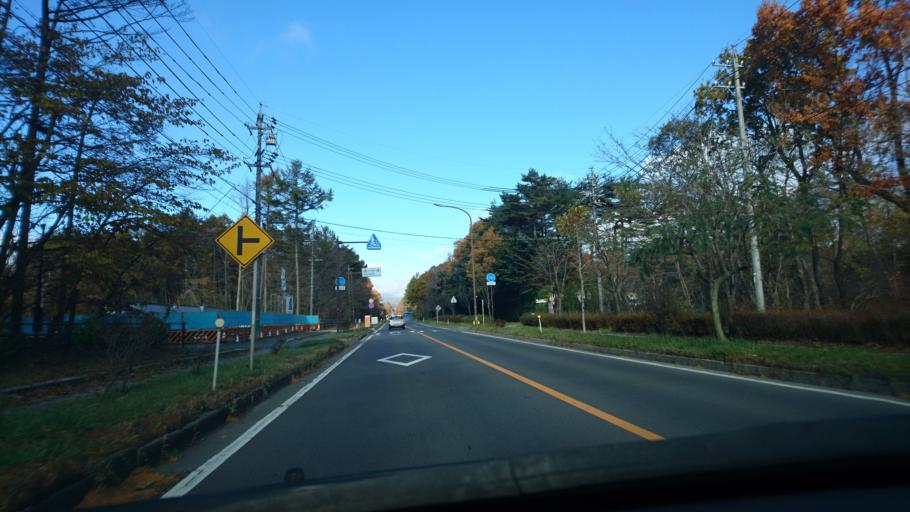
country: JP
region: Nagano
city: Saku
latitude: 36.3249
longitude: 138.6211
